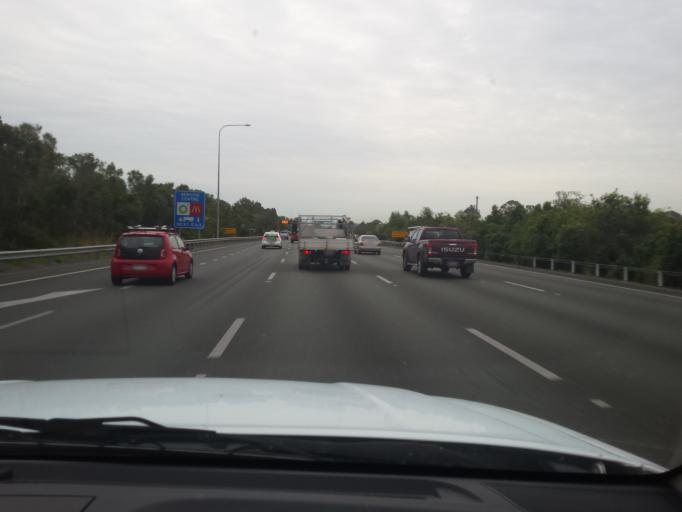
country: AU
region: Queensland
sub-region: Gold Coast
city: Oxenford
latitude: -27.8791
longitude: 153.3148
